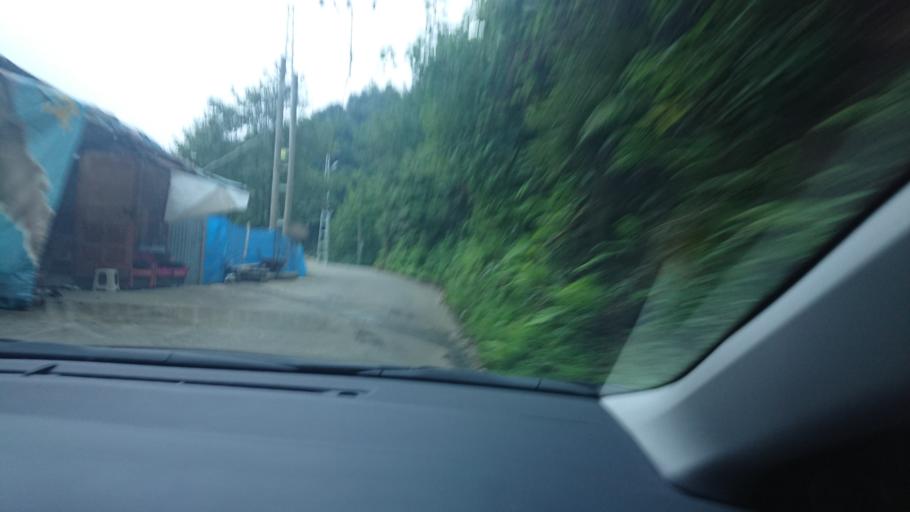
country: TR
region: Rize
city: Cayeli
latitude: 41.0484
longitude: 40.7981
